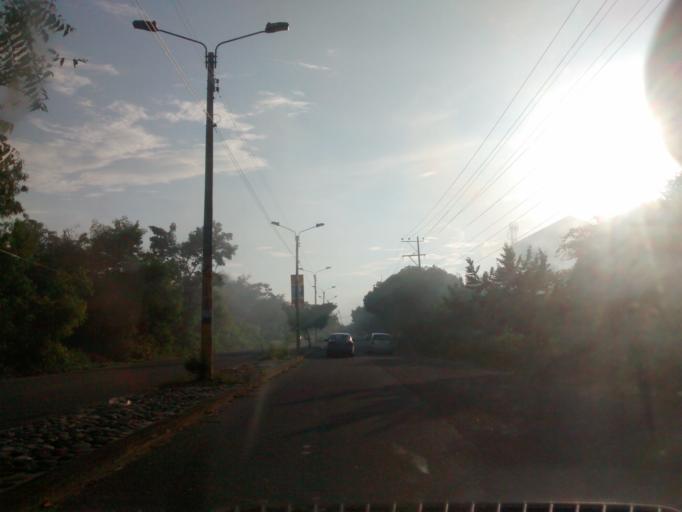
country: CO
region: Tolima
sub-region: Flandes
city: Flandes
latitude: 4.2996
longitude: -74.8193
